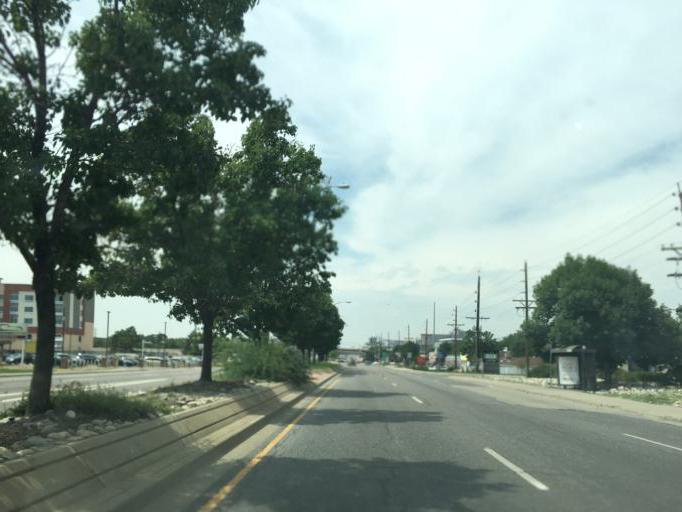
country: US
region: Colorado
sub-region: Adams County
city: Aurora
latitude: 39.7403
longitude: -104.8197
